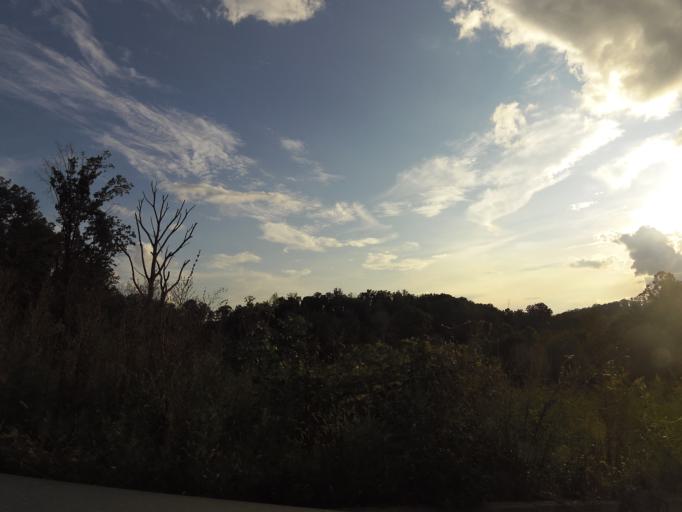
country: US
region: Tennessee
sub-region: Knox County
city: Knoxville
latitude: 36.0040
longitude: -84.0006
